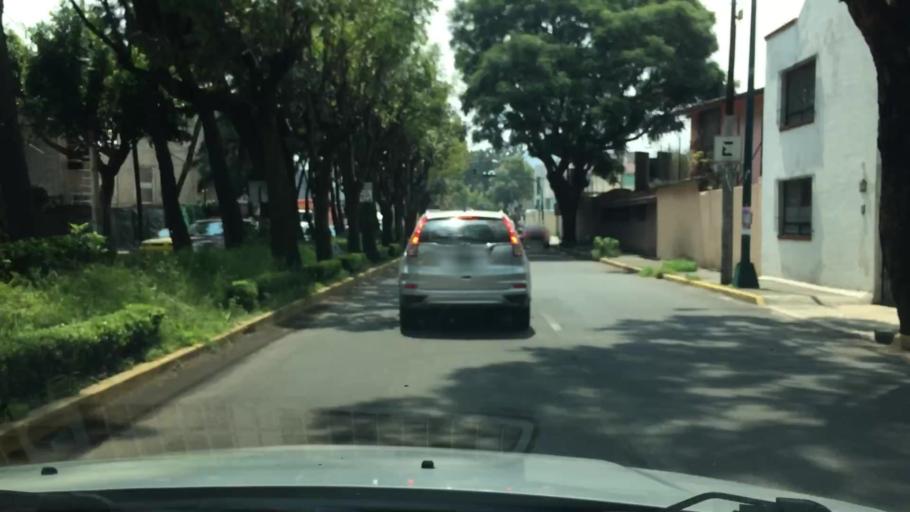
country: MX
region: Mexico City
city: Xochimilco
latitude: 19.2806
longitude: -99.1262
